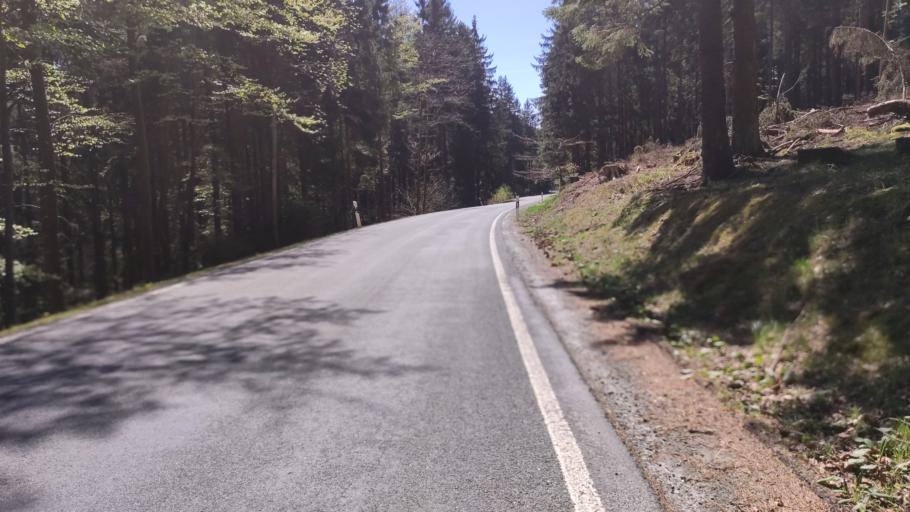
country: DE
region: Bavaria
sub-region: Upper Franconia
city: Tschirn
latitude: 50.4533
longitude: 11.4621
